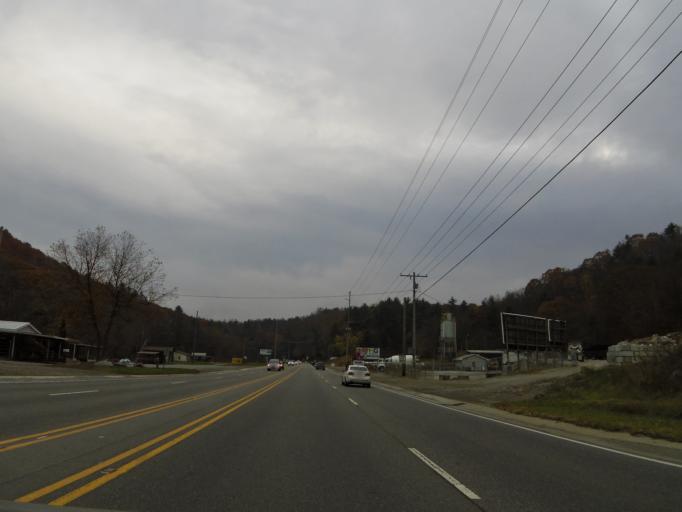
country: US
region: North Carolina
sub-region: Watauga County
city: Boone
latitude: 36.1795
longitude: -81.6474
